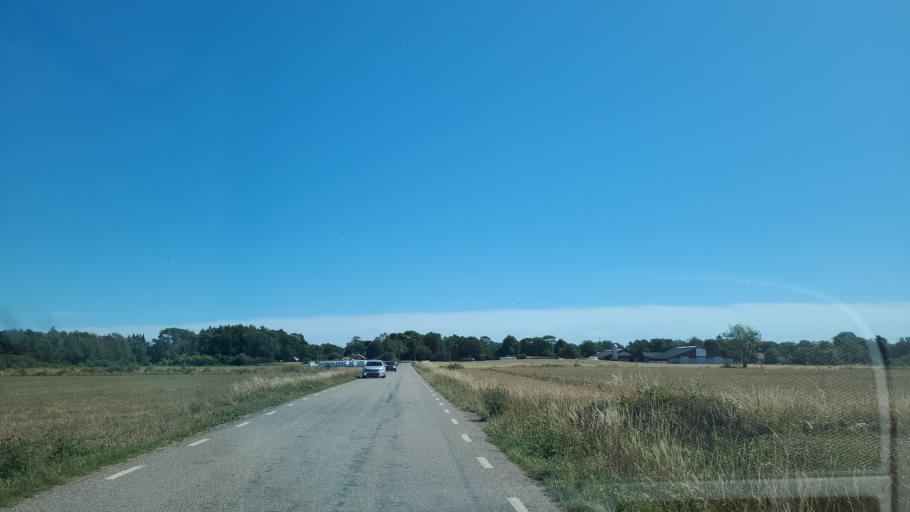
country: SE
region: Kalmar
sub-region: Borgholms Kommun
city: Borgholm
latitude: 56.7398
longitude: 16.7157
